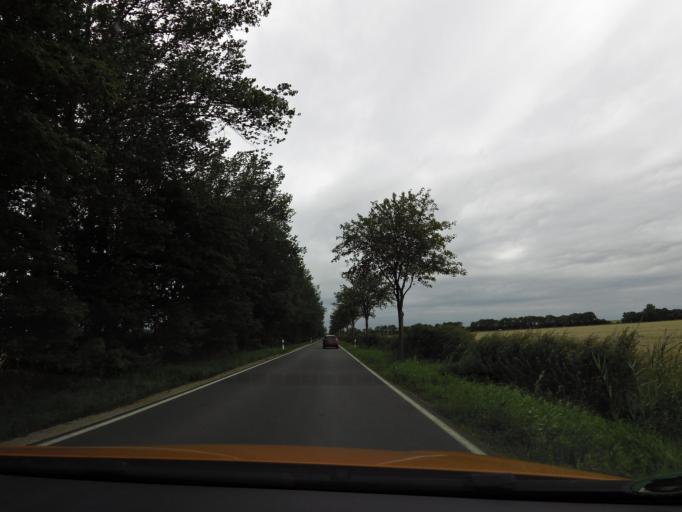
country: DE
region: Lower Saxony
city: Wirdum
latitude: 53.5160
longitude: 7.1363
